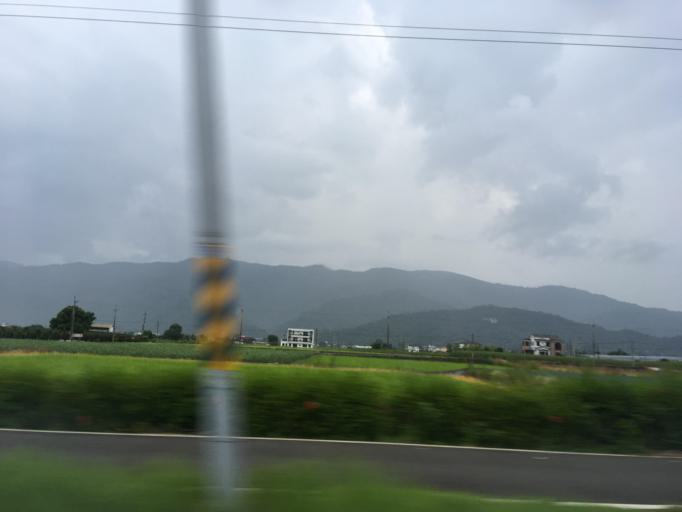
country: TW
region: Taiwan
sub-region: Yilan
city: Yilan
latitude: 24.6772
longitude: 121.6455
